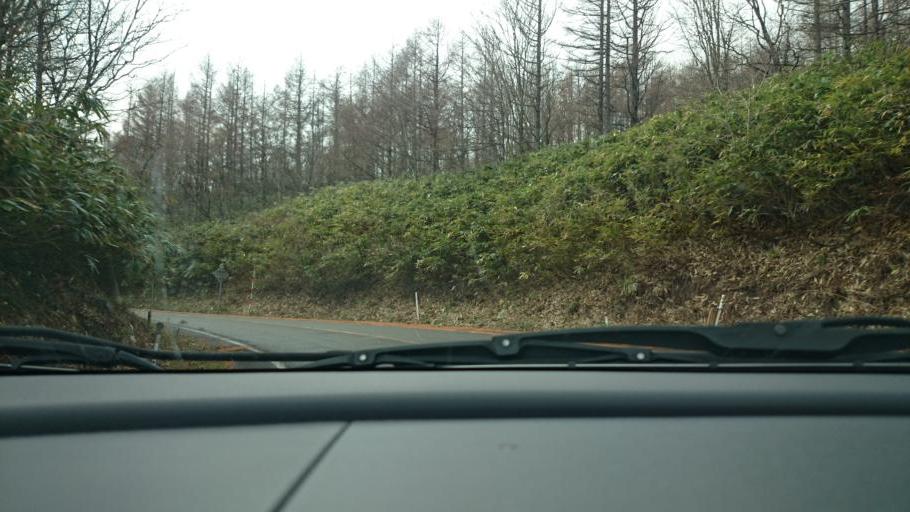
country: JP
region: Tochigi
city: Kuroiso
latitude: 37.1440
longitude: 140.0120
